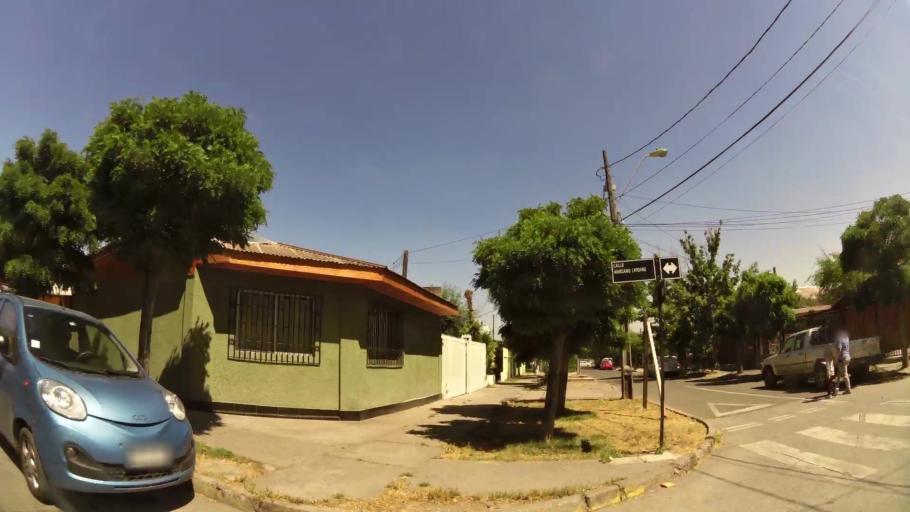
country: CL
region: Santiago Metropolitan
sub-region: Provincia de Maipo
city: San Bernardo
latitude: -33.5621
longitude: -70.6754
